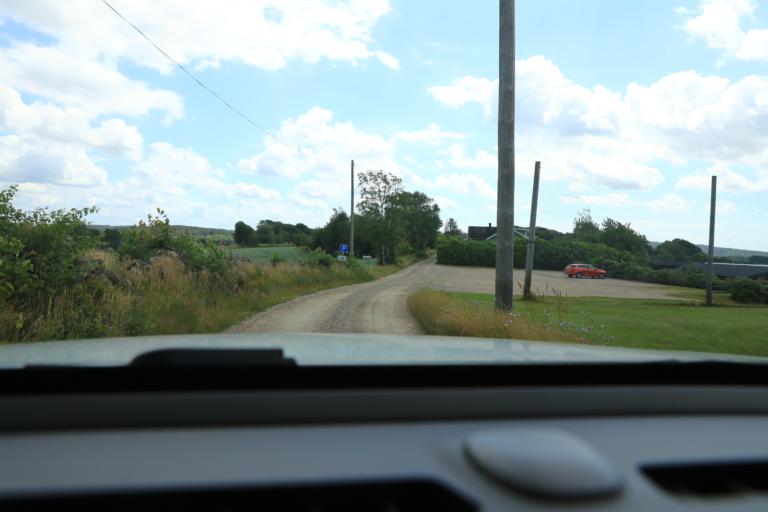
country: SE
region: Halland
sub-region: Varbergs Kommun
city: Tvaaker
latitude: 57.1099
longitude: 12.4126
